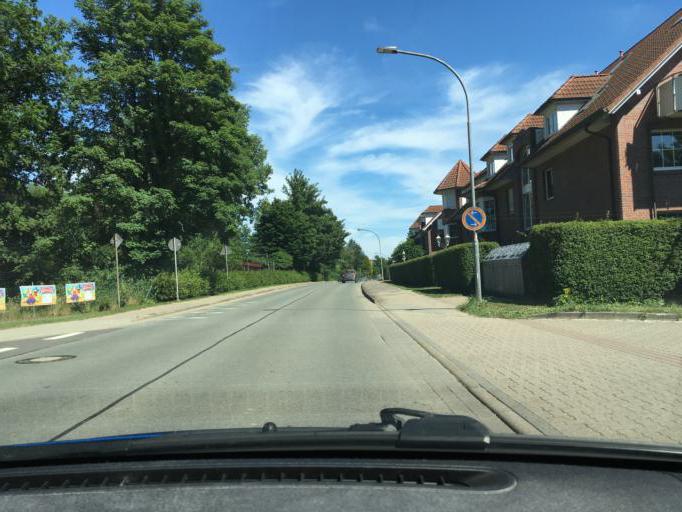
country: DE
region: Lower Saxony
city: Bendestorf
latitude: 53.3683
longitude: 9.9191
